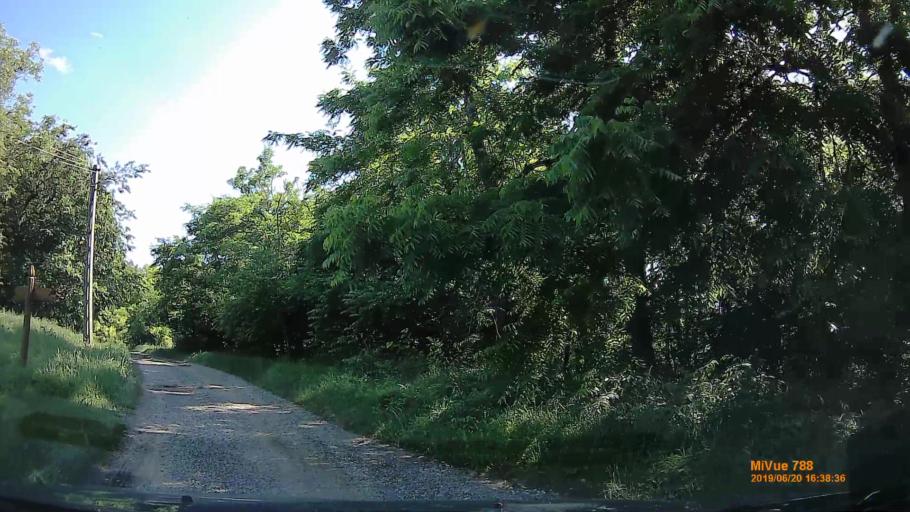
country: HU
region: Baranya
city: Buekkoesd
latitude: 46.1715
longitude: 18.0326
